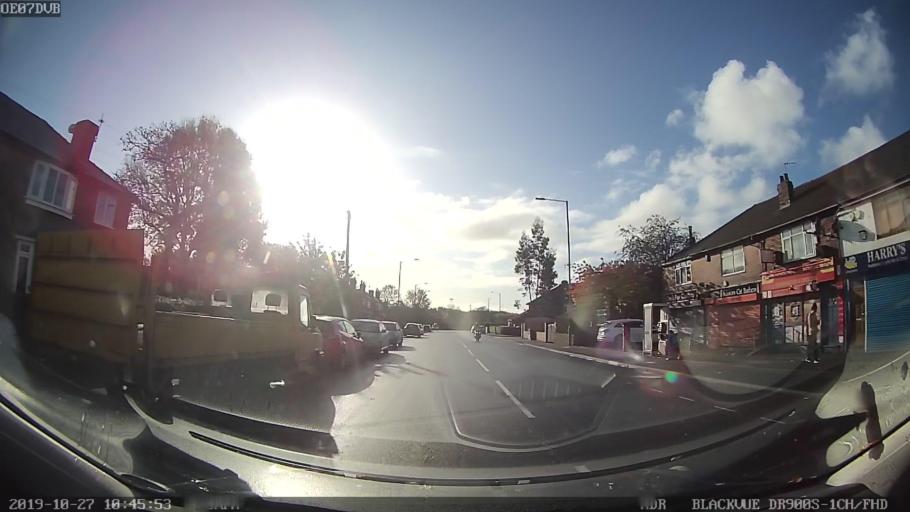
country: GB
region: England
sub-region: Manchester
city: Failsworth
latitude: 53.5209
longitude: -2.1820
